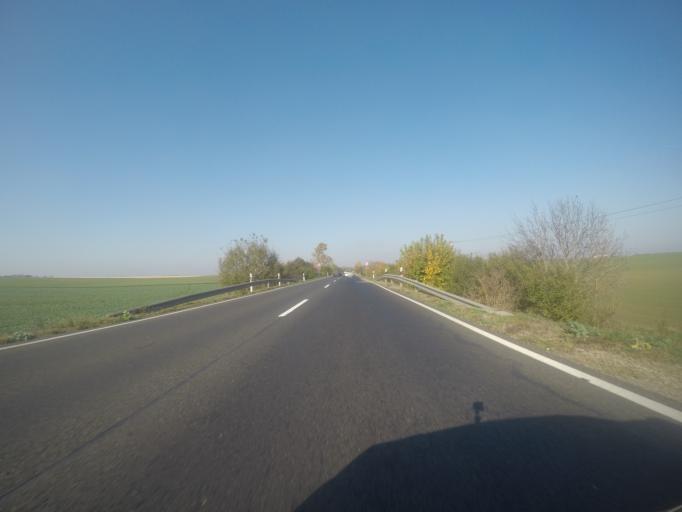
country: HU
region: Fejer
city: Baracs
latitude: 46.8849
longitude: 18.9191
